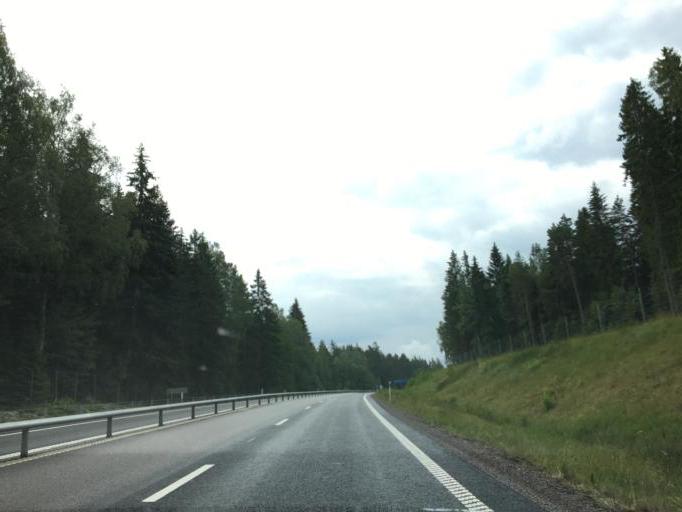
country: SE
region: Soedermanland
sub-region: Katrineholms Kommun
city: Katrineholm
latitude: 58.9019
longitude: 16.2054
